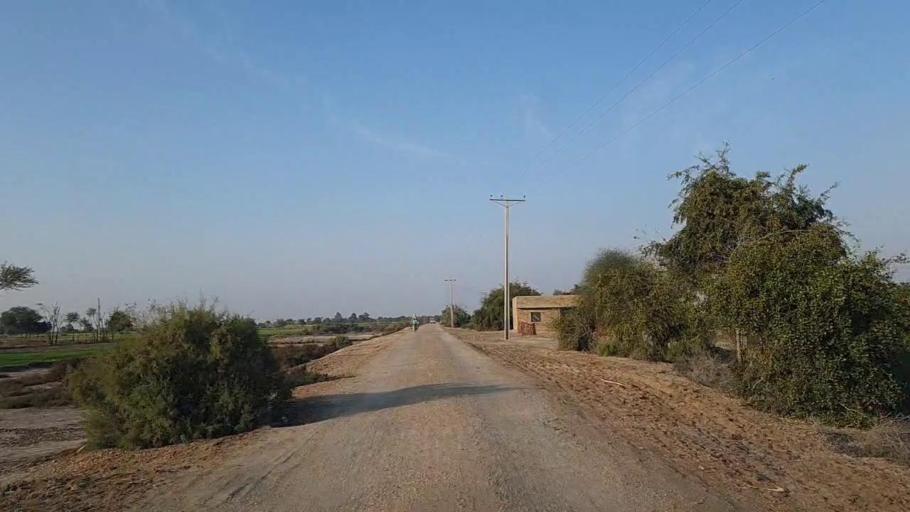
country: PK
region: Sindh
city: Jam Sahib
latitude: 26.3801
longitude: 68.5389
